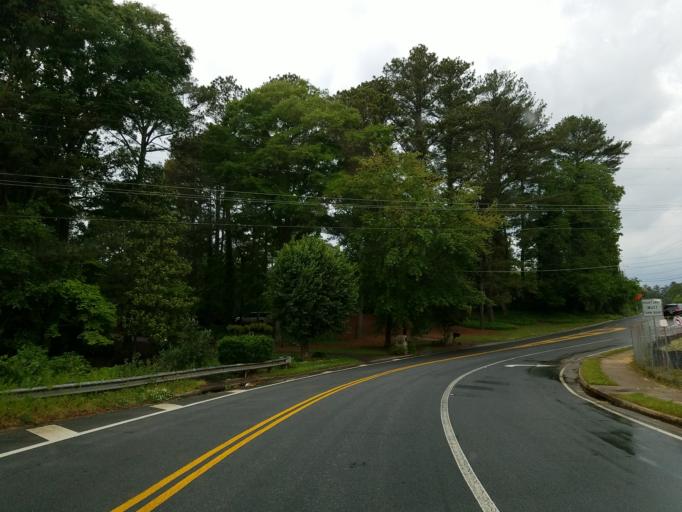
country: US
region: Georgia
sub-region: Fulton County
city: Roswell
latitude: 33.9875
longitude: -84.4407
